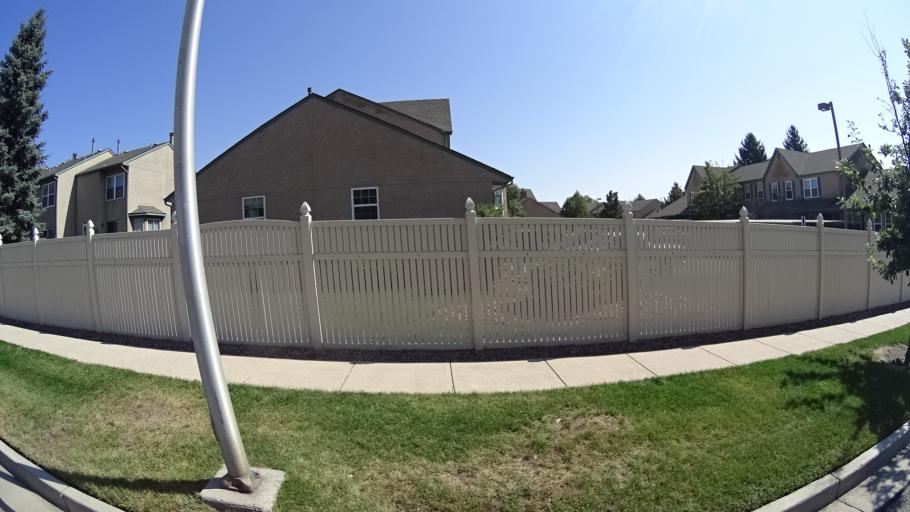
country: US
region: Colorado
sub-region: El Paso County
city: Air Force Academy
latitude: 38.9196
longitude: -104.8260
